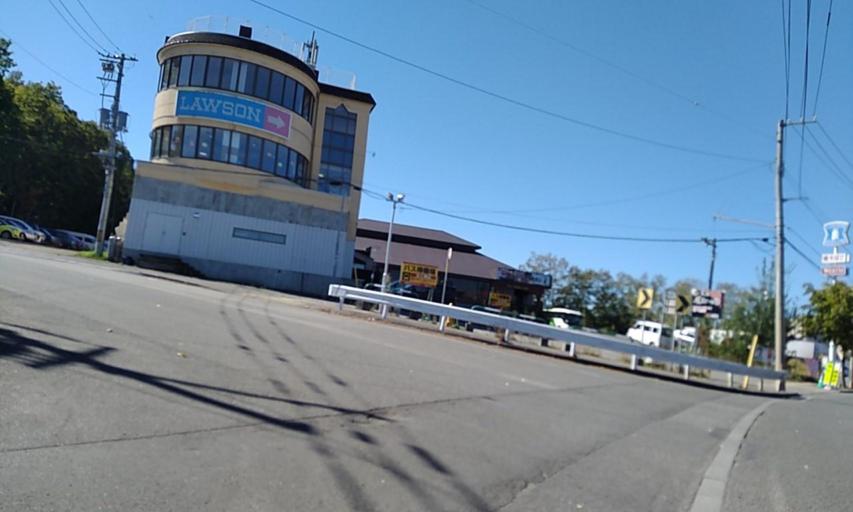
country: JP
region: Hokkaido
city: Sapporo
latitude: 43.0031
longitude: 141.3933
